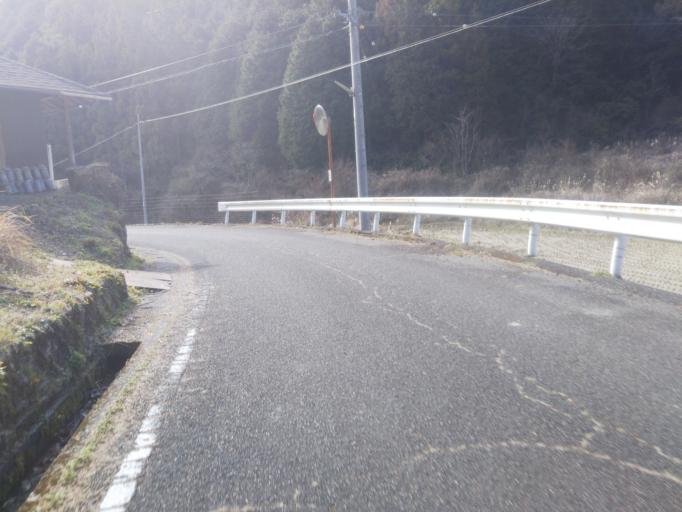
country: JP
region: Kochi
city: Nakamura
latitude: 33.0426
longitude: 132.9854
